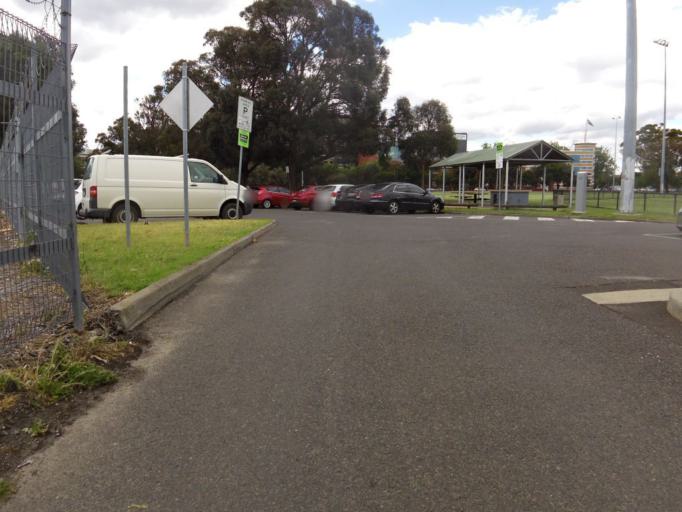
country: AU
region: Victoria
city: Glen Huntly
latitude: -37.8796
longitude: 145.0464
